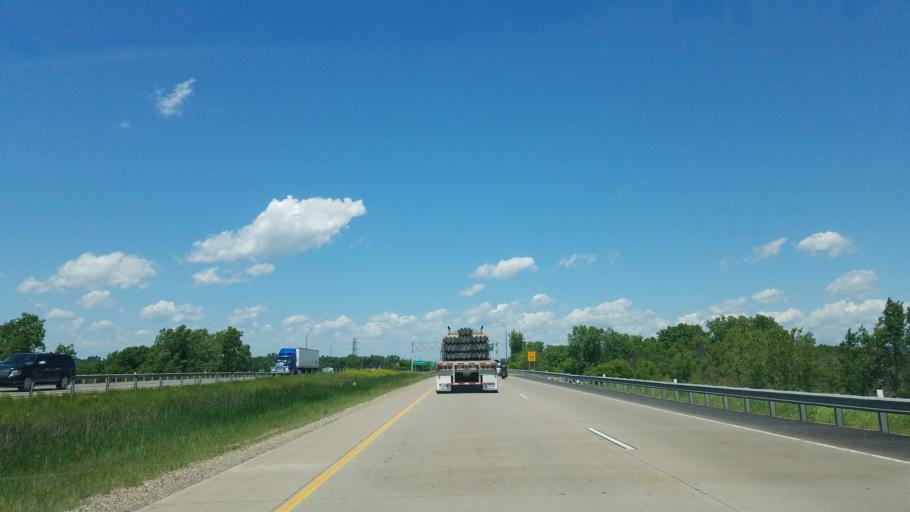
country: US
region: Minnesota
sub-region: Ramsey County
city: North Saint Paul
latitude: 45.0244
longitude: -92.9597
